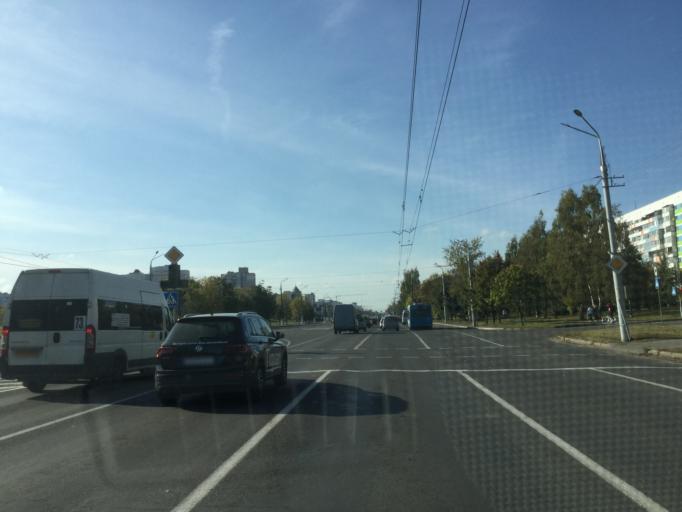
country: BY
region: Vitebsk
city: Vitebsk
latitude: 55.1695
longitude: 30.2324
